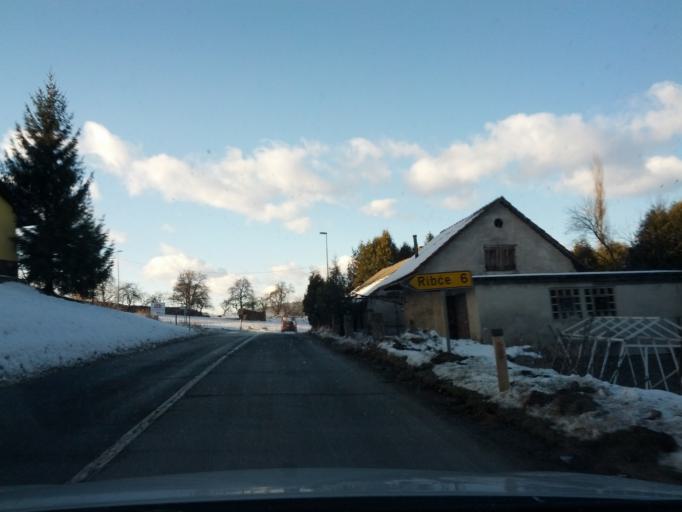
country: SI
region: Moravce
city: Moravce
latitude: 46.1298
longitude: 14.7497
